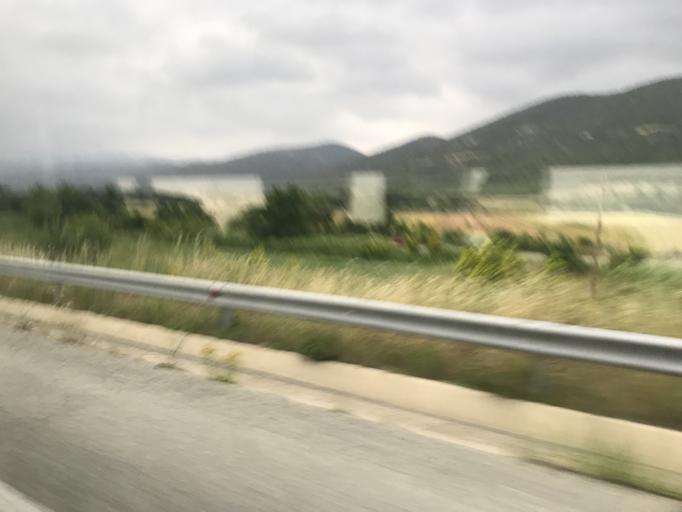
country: GR
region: East Macedonia and Thrace
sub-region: Nomos Xanthis
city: Selero
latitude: 41.1197
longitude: 25.0888
